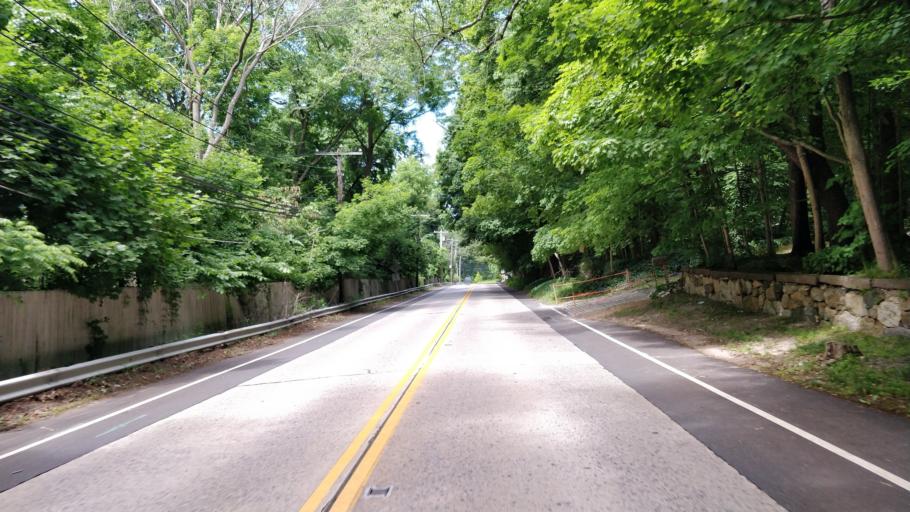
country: US
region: New York
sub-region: Nassau County
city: Laurel Hollow
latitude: 40.8484
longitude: -73.4747
